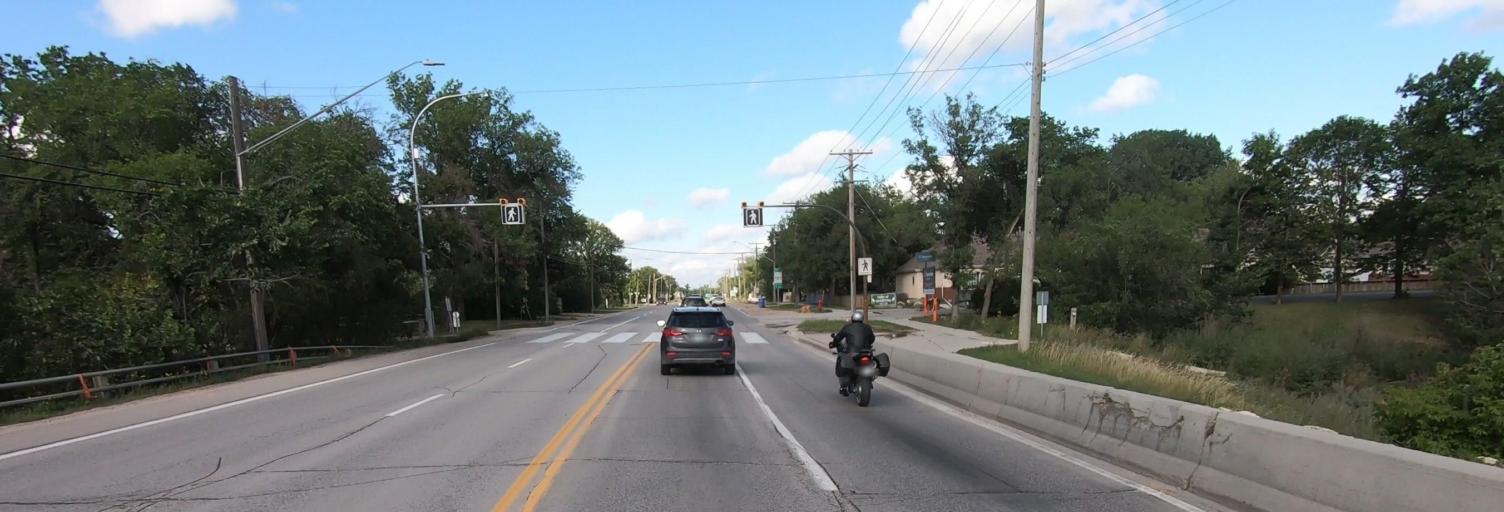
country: CA
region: Manitoba
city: Winnipeg
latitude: 49.9588
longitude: -97.0701
